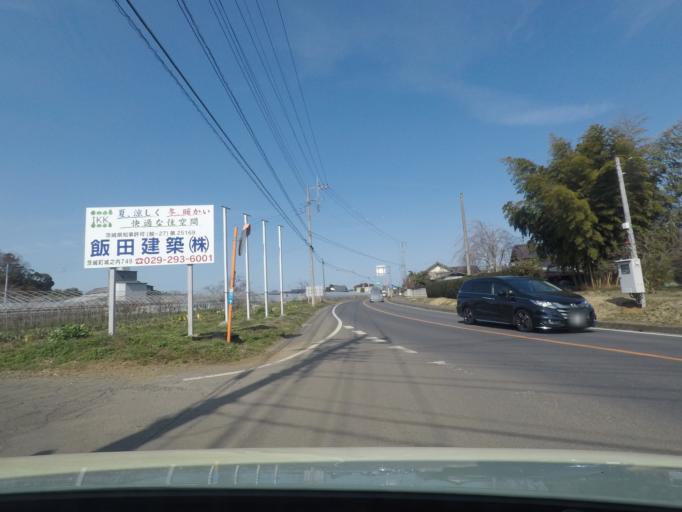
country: JP
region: Ibaraki
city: Okunoya
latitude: 36.2389
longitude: 140.4493
